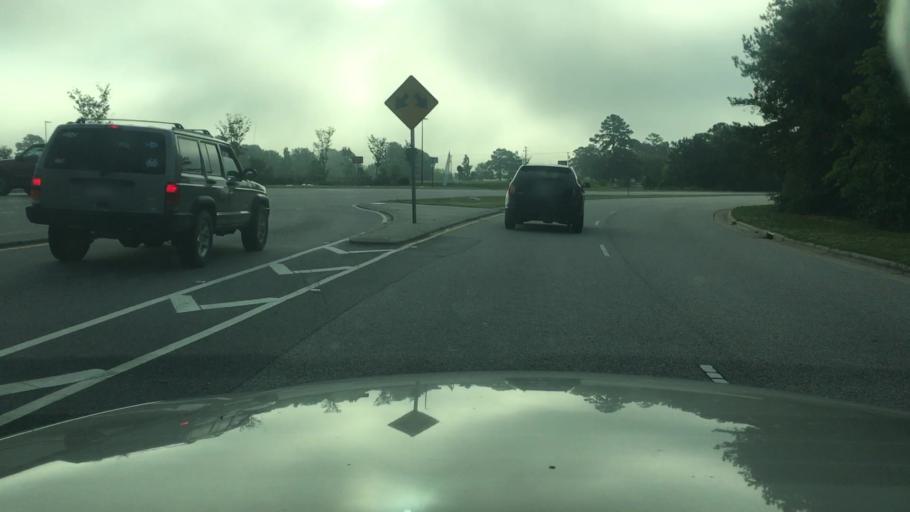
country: US
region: North Carolina
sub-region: Cumberland County
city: Hope Mills
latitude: 35.0011
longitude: -78.9022
